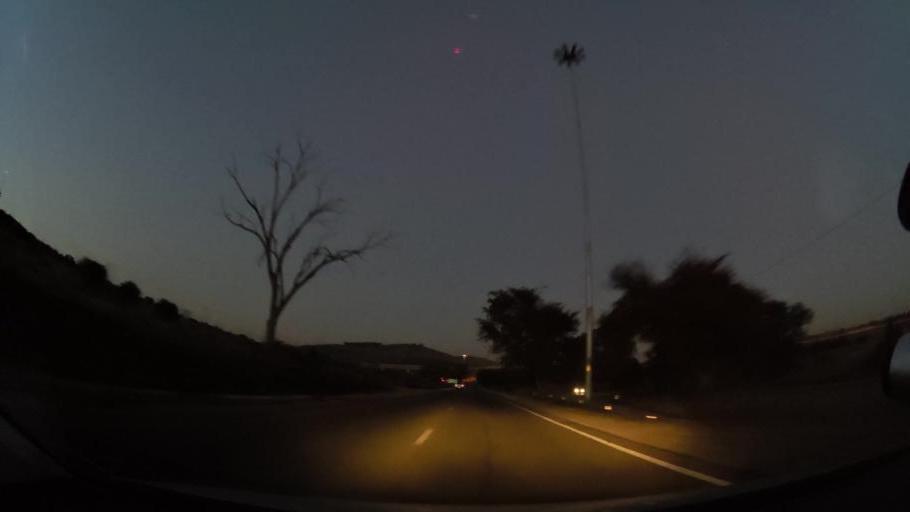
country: ZA
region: Gauteng
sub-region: City of Tshwane Metropolitan Municipality
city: Pretoria
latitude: -25.7831
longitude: 28.1834
